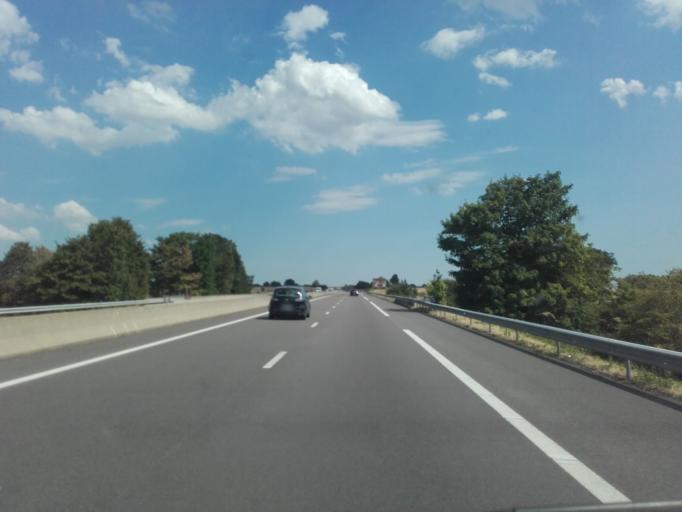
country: FR
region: Bourgogne
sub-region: Departement de la Cote-d'Or
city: Semur-en-Auxois
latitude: 47.4777
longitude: 4.1931
